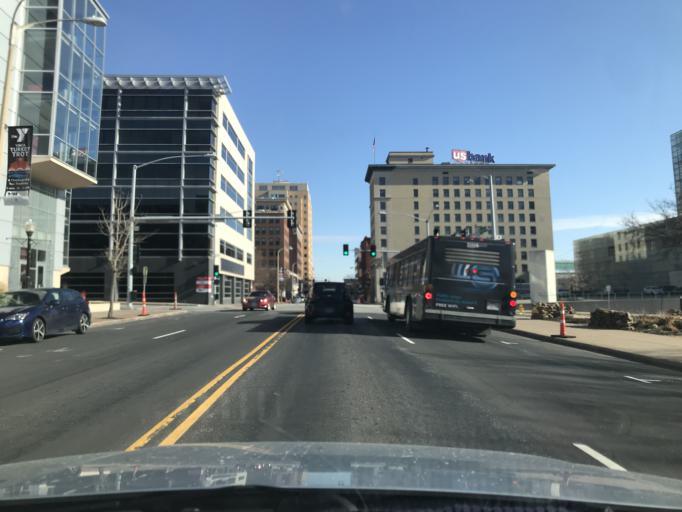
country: US
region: Iowa
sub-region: Scott County
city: Davenport
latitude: 41.5213
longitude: -90.5776
